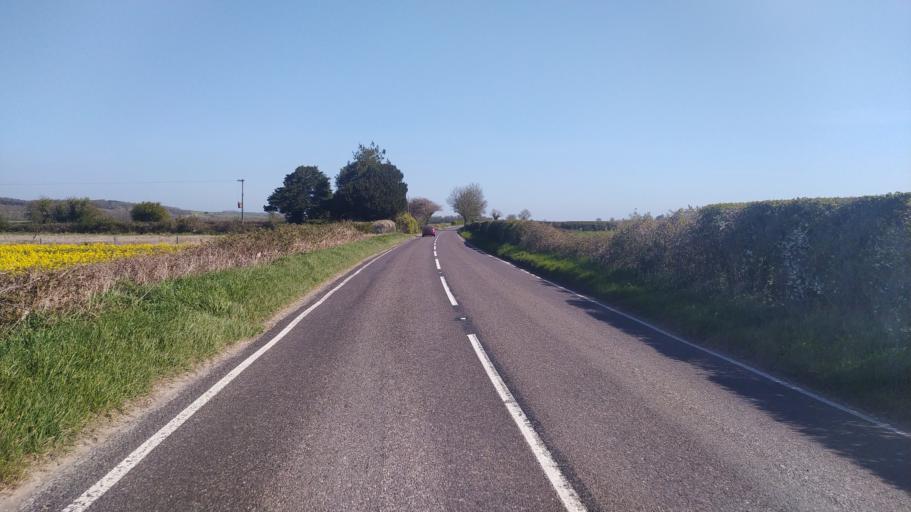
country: GB
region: England
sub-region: Dorset
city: Wimborne Minster
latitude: 50.8559
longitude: -1.9969
